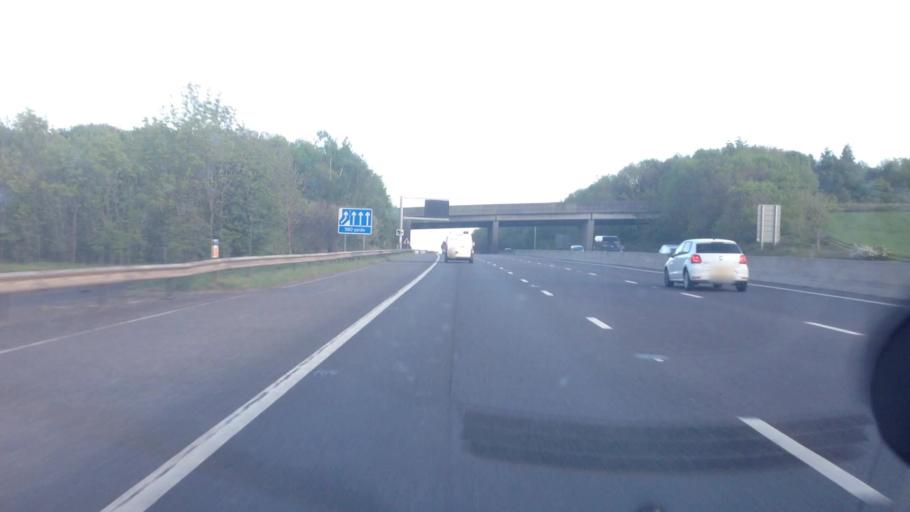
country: GB
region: England
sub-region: Sheffield
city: Chapletown
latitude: 53.4806
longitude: -1.4639
